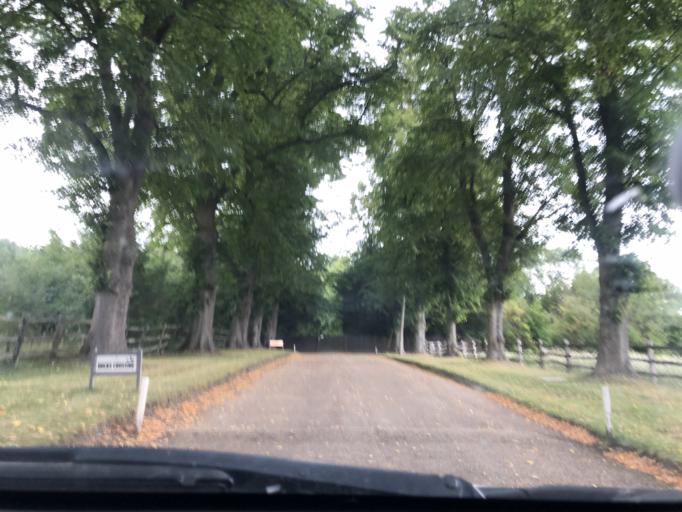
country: GB
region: England
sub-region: Kent
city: Swanley
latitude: 51.4159
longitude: 0.1879
